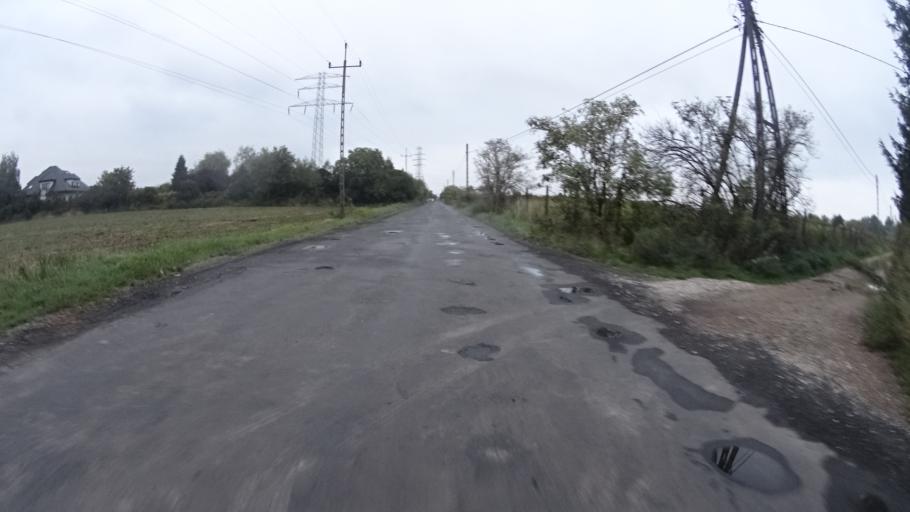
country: PL
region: Masovian Voivodeship
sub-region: Warszawa
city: Ursus
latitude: 52.2217
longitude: 20.8760
